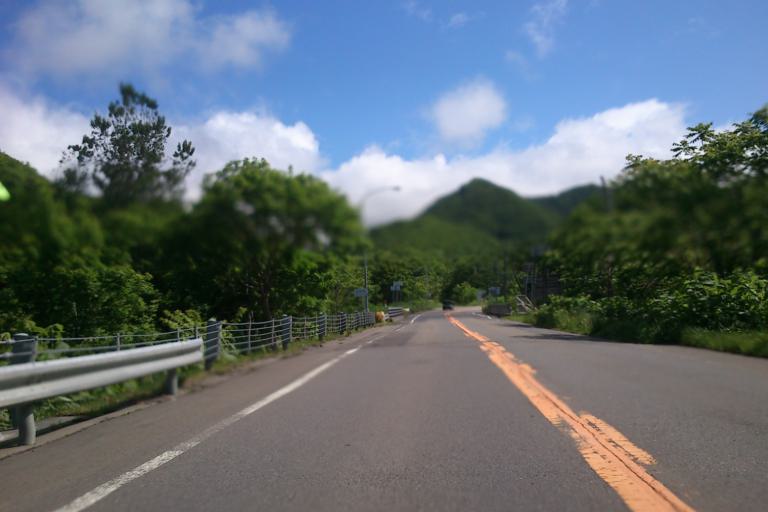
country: JP
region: Hokkaido
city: Ishikari
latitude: 43.4809
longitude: 141.3972
